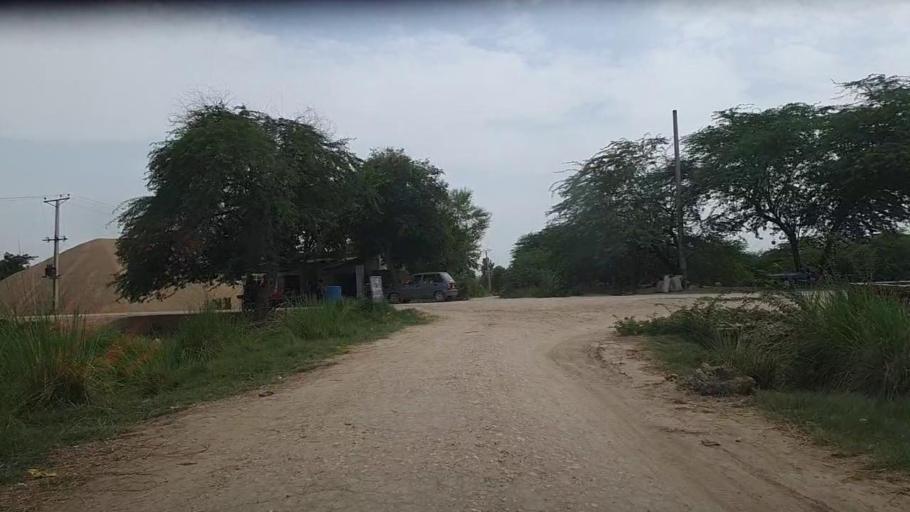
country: PK
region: Sindh
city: Bhiria
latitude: 26.8836
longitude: 68.2954
